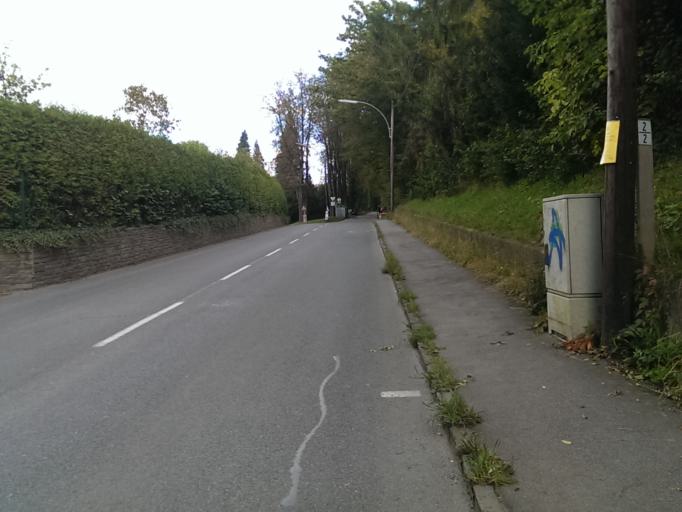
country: AT
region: Styria
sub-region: Graz Stadt
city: Mariatrost
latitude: 47.0699
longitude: 15.4904
